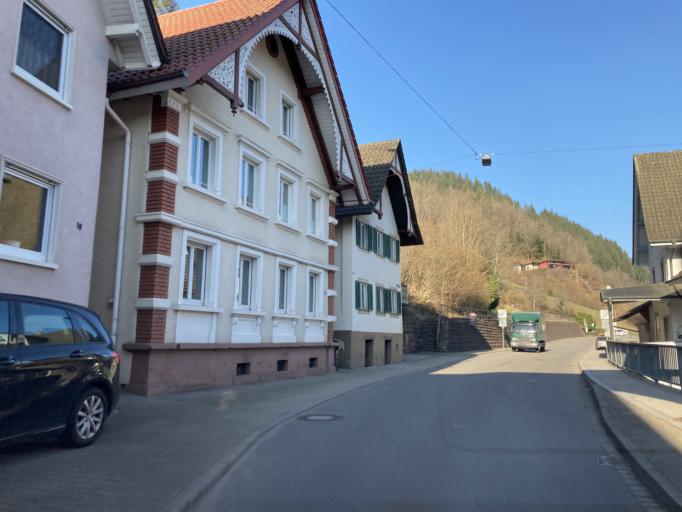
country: DE
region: Baden-Wuerttemberg
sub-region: Freiburg Region
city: Oppenau
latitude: 48.4767
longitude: 8.1686
